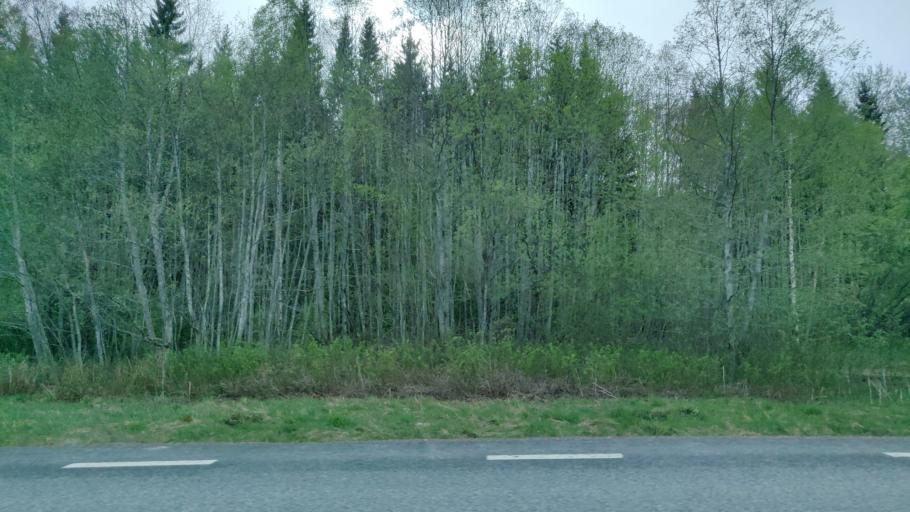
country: SE
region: Vaermland
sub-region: Munkfors Kommun
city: Munkfors
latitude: 59.7680
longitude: 13.4383
